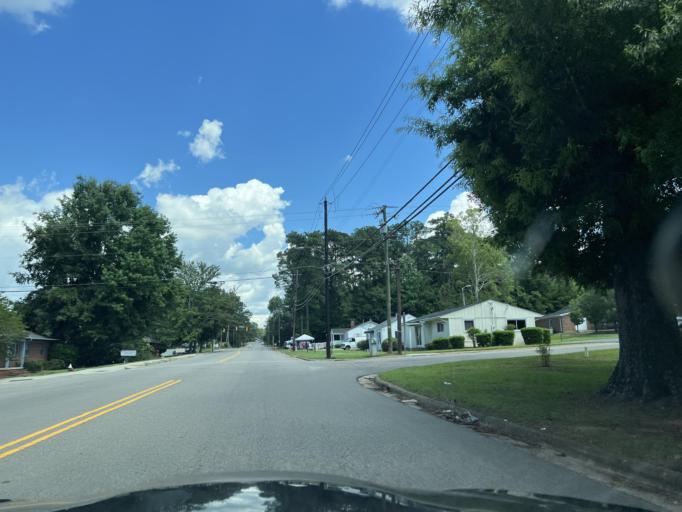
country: US
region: North Carolina
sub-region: Lee County
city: Sanford
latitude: 35.4665
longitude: -79.1657
